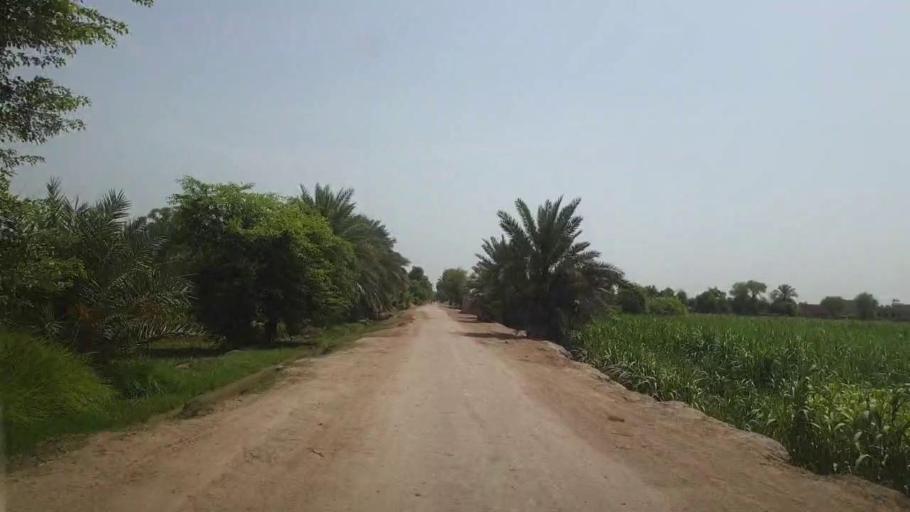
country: PK
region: Sindh
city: Sobhadero
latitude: 27.4403
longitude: 68.4025
